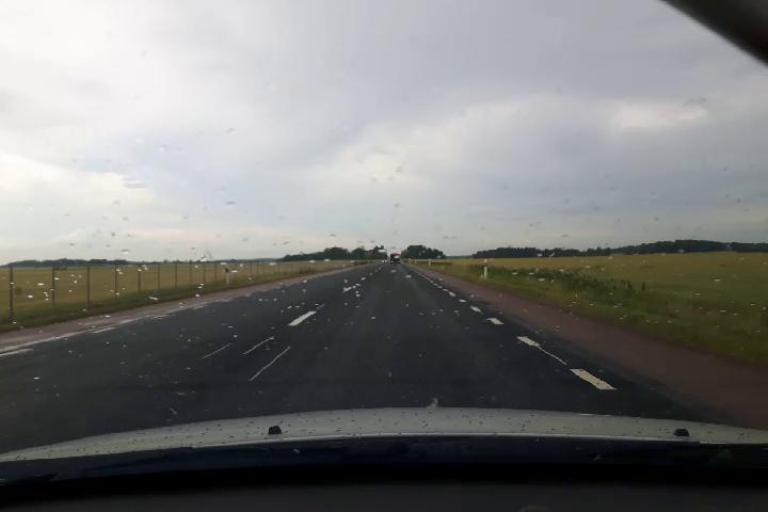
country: SE
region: Uppsala
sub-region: Uppsala Kommun
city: Gamla Uppsala
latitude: 59.9511
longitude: 17.5879
